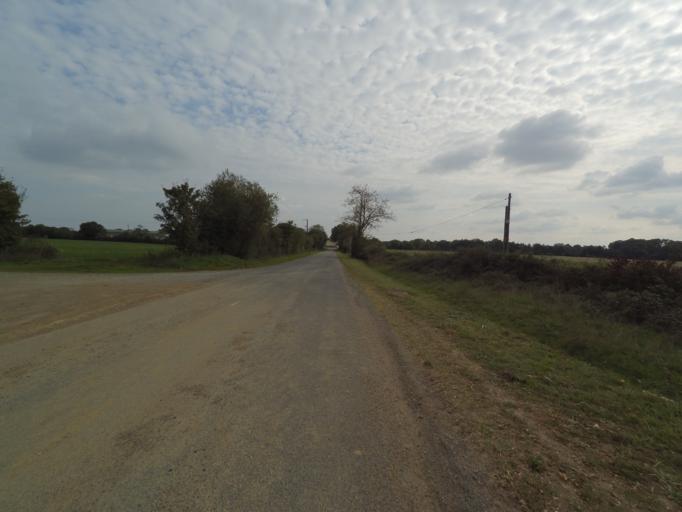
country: FR
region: Pays de la Loire
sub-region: Departement de la Vendee
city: Bouffere
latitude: 46.9837
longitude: -1.3534
